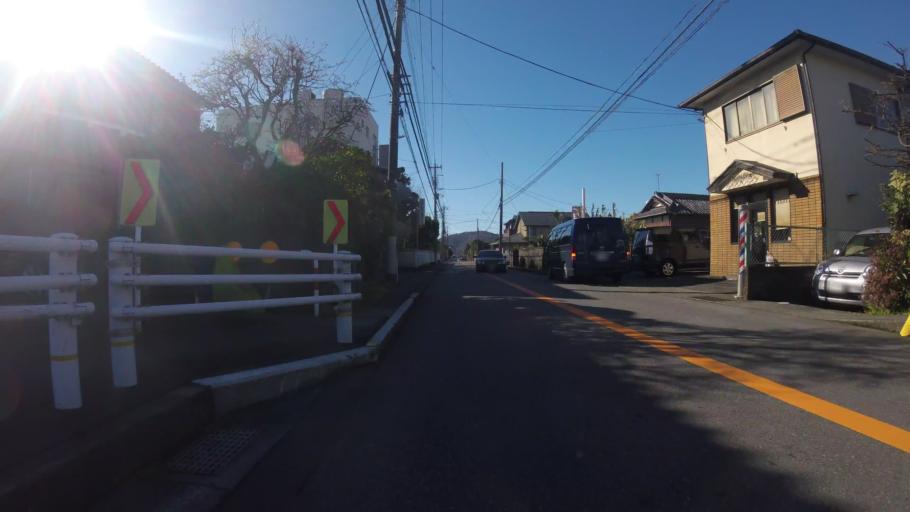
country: JP
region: Shizuoka
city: Mishima
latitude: 35.1128
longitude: 138.9003
